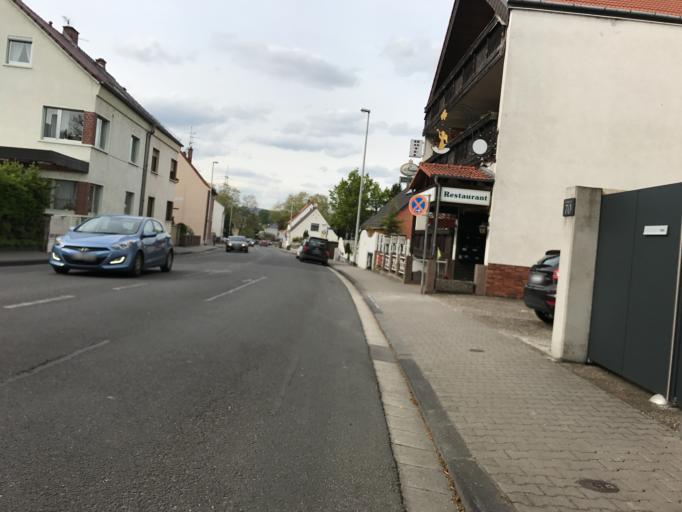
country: DE
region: Rheinland-Pfalz
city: Budenheim
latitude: 50.0210
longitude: 8.2207
